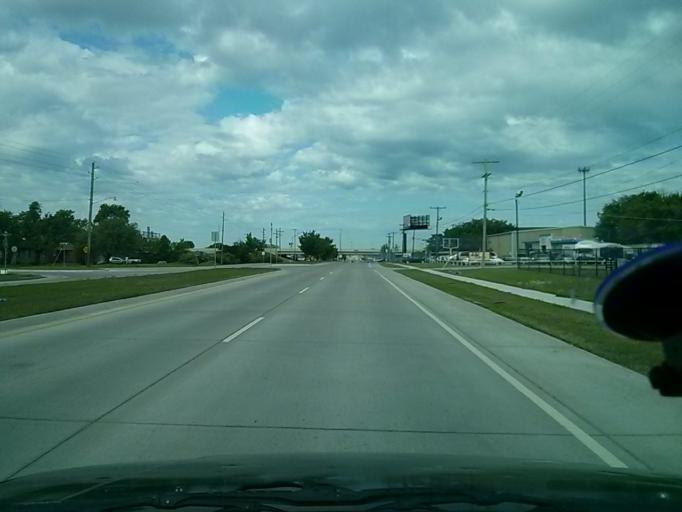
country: US
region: Oklahoma
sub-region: Tulsa County
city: Owasso
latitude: 36.1608
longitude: -95.8572
